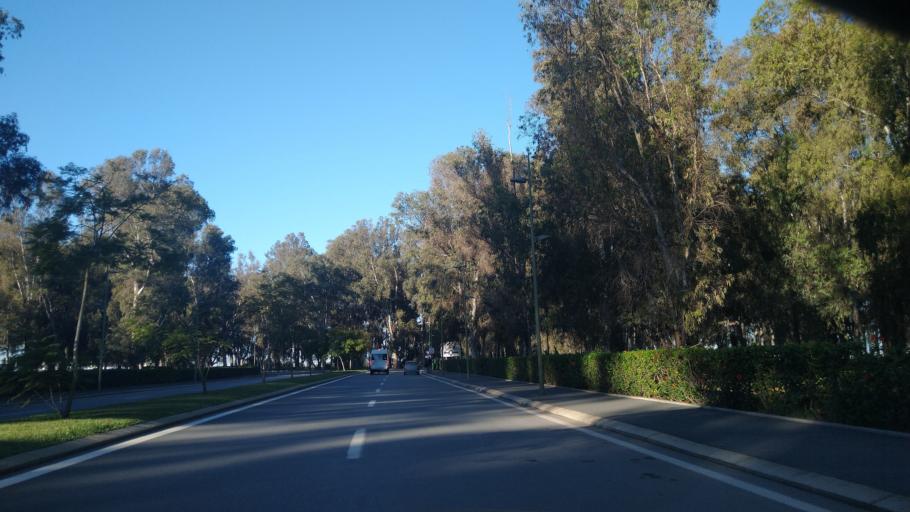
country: MA
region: Rabat-Sale-Zemmour-Zaer
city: Sale
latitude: 34.0340
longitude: -6.7505
